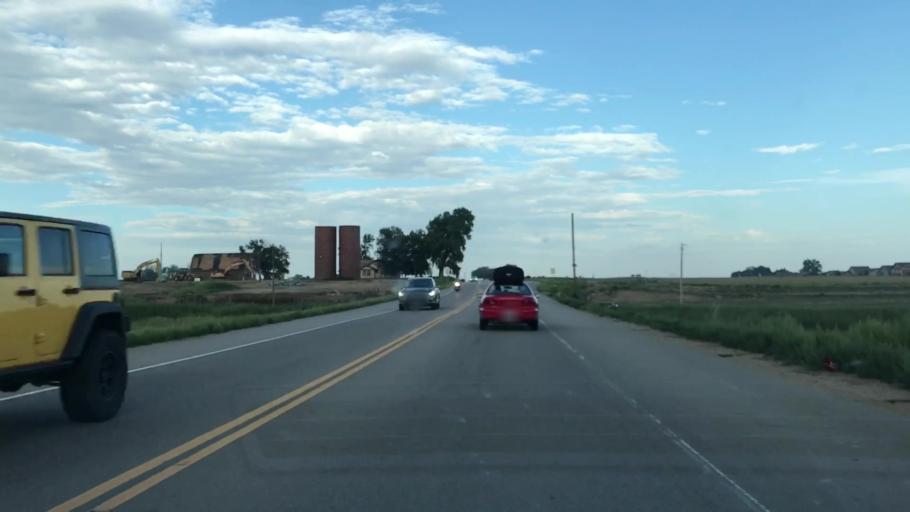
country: US
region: Colorado
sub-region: Weld County
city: Mead
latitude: 40.2040
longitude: -105.0095
